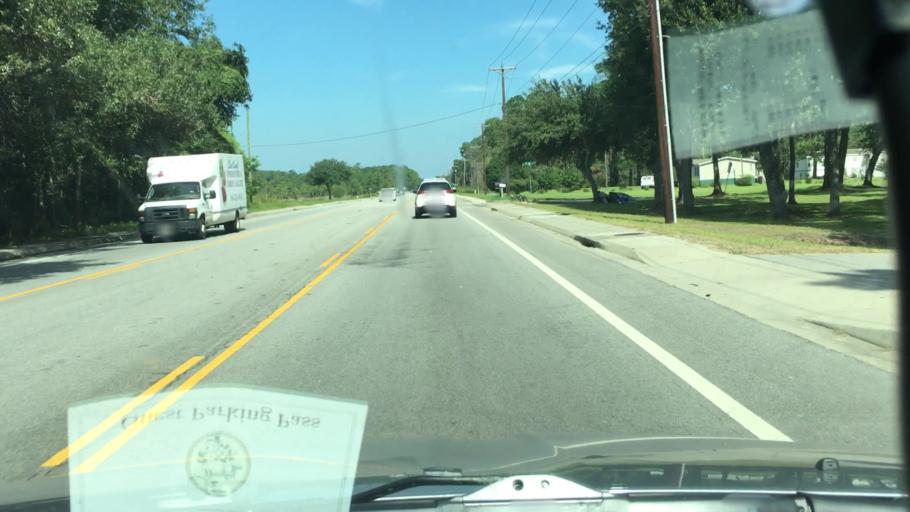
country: US
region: South Carolina
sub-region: Beaufort County
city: Beaufort
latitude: 32.4027
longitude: -80.6280
